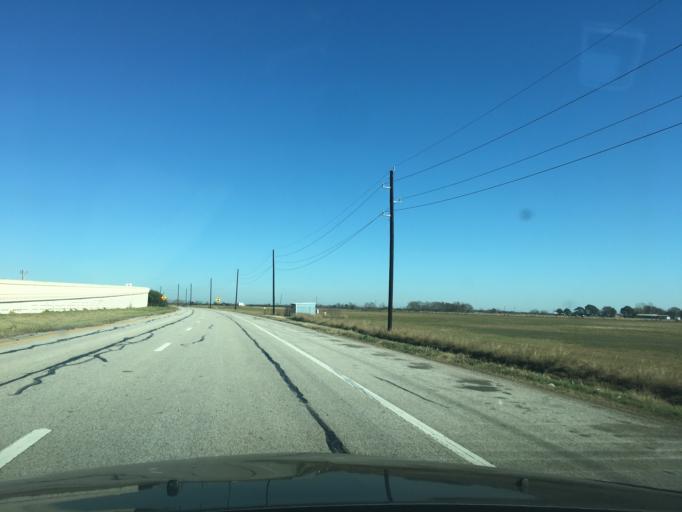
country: US
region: Texas
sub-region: Fort Bend County
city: Pleak
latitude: 29.4921
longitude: -95.9154
